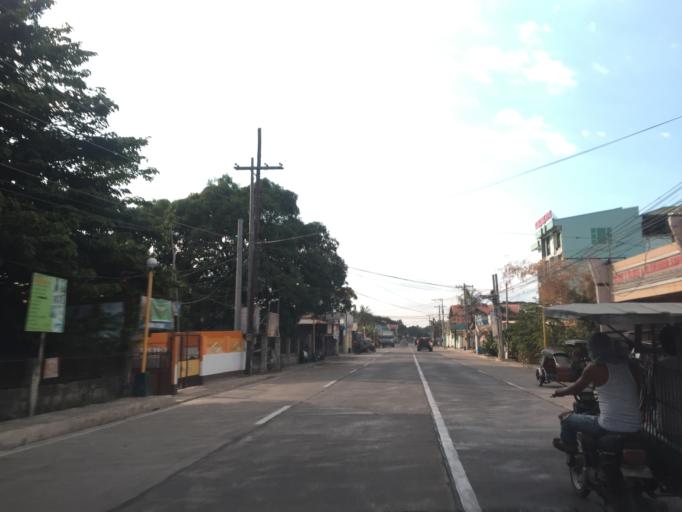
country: PH
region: Ilocos
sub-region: Province of Pangasinan
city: Bolingit
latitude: 15.9367
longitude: 120.3466
